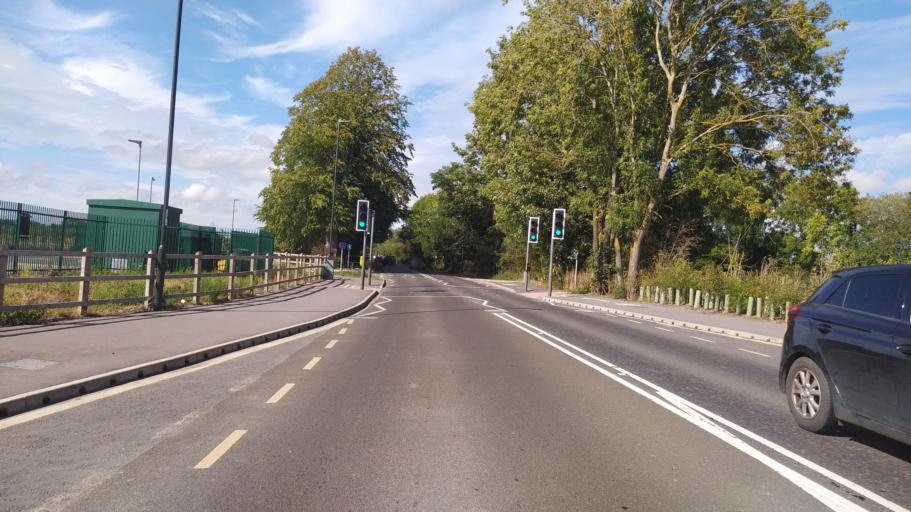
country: GB
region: England
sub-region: West Sussex
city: Chichester
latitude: 50.8225
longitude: -0.7681
